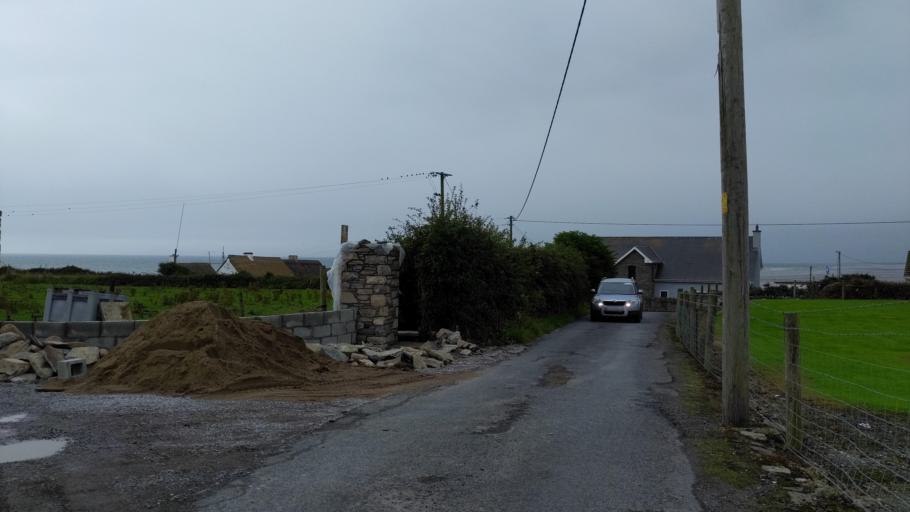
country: IE
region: Leinster
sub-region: Lu
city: Clogherhead
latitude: 53.7901
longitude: -6.2342
